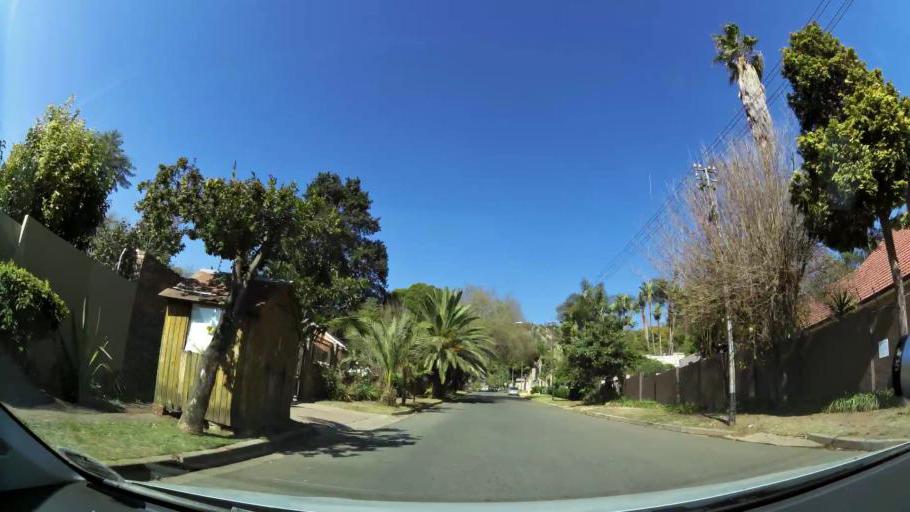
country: ZA
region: Gauteng
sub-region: City of Johannesburg Metropolitan Municipality
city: Johannesburg
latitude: -26.1644
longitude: 28.1026
